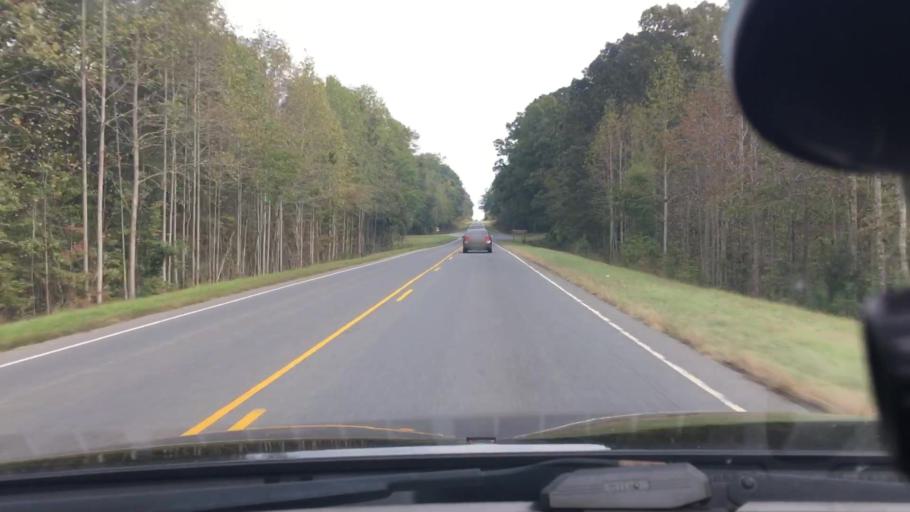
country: US
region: North Carolina
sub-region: Montgomery County
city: Mount Gilead
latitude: 35.3115
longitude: -80.0461
